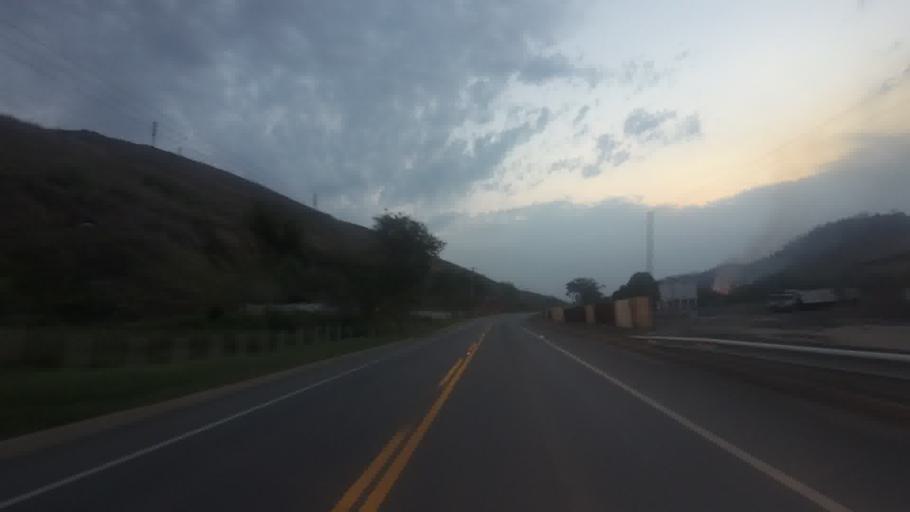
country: BR
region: Minas Gerais
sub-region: Alem Paraiba
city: Alem Paraiba
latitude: -21.9032
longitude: -42.7275
